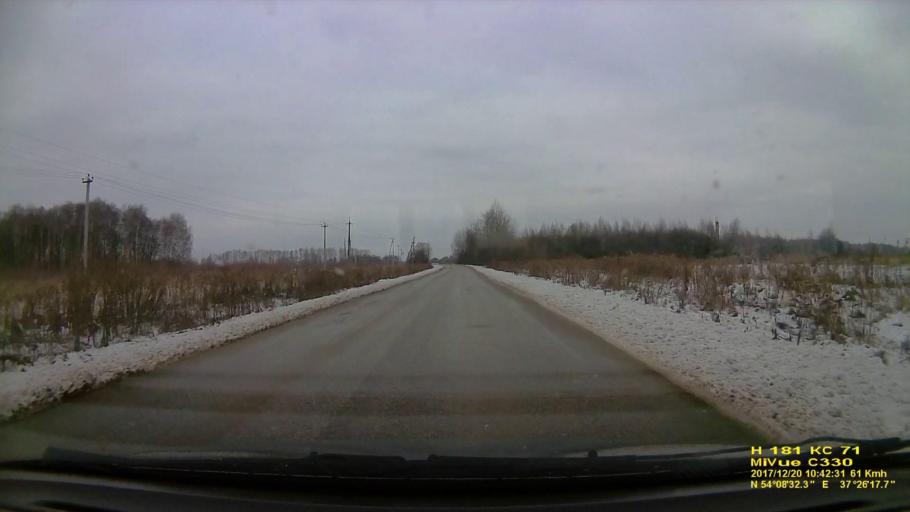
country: RU
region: Tula
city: Kosaya Gora
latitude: 54.1425
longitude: 37.4382
